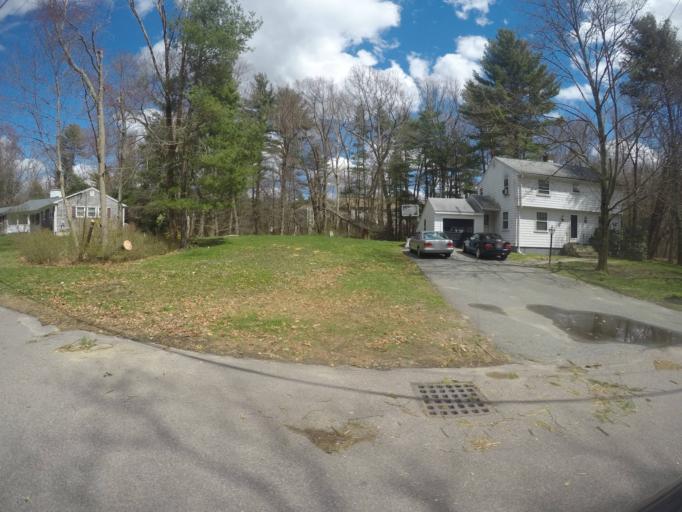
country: US
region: Massachusetts
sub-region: Bristol County
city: Easton
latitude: 42.0288
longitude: -71.0725
